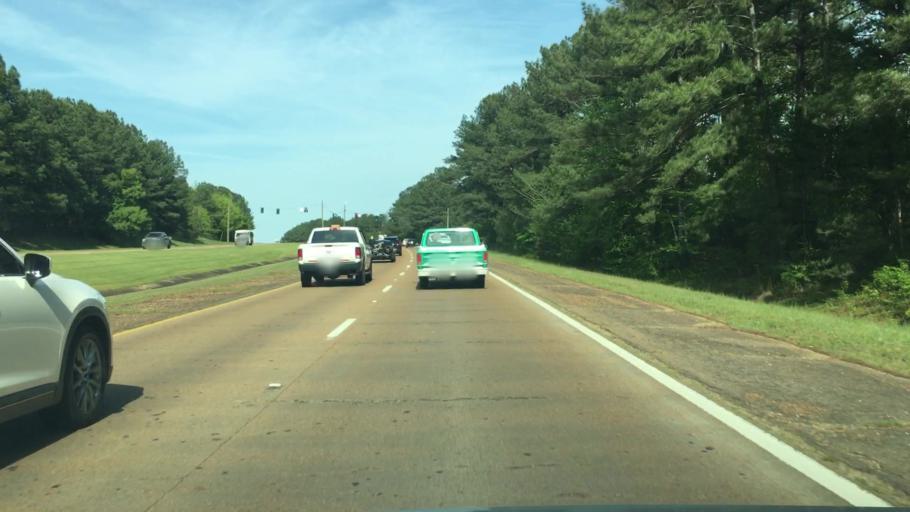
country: US
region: Mississippi
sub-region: Rankin County
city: Brandon
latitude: 32.3613
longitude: -89.9965
